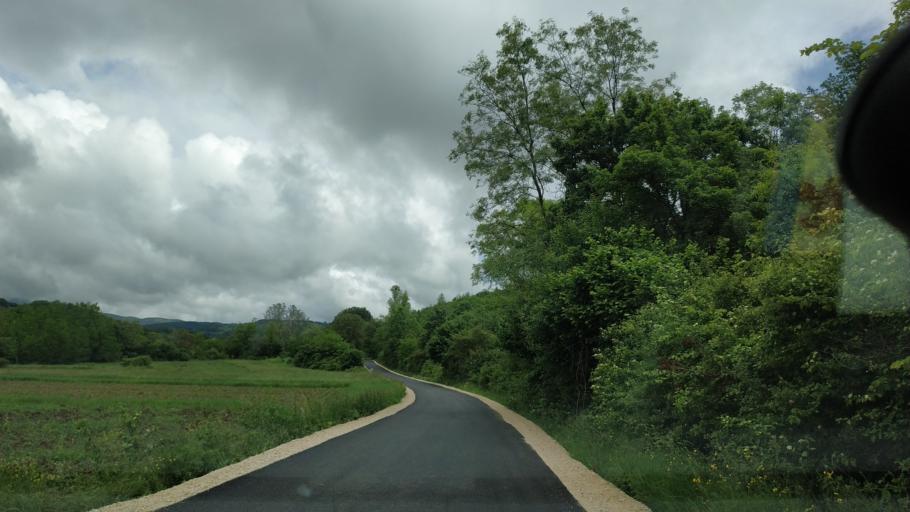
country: RS
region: Central Serbia
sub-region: Zajecarski Okrug
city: Soko Banja
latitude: 43.6605
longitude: 21.9092
